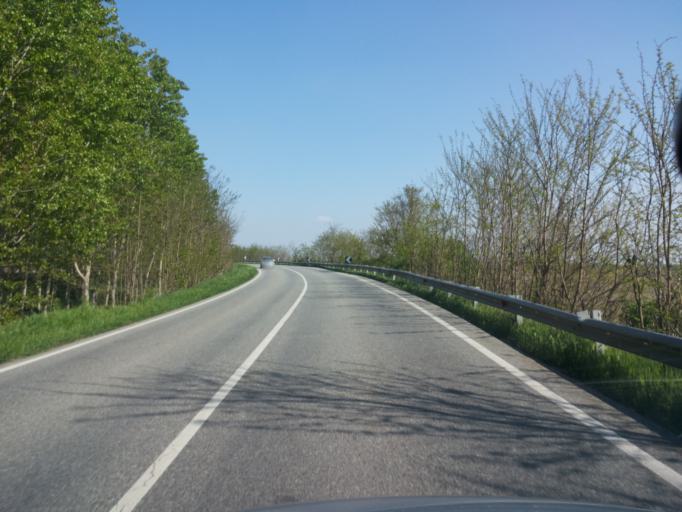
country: IT
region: Piedmont
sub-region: Provincia di Vercelli
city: Motta De Conti
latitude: 45.2054
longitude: 8.5377
